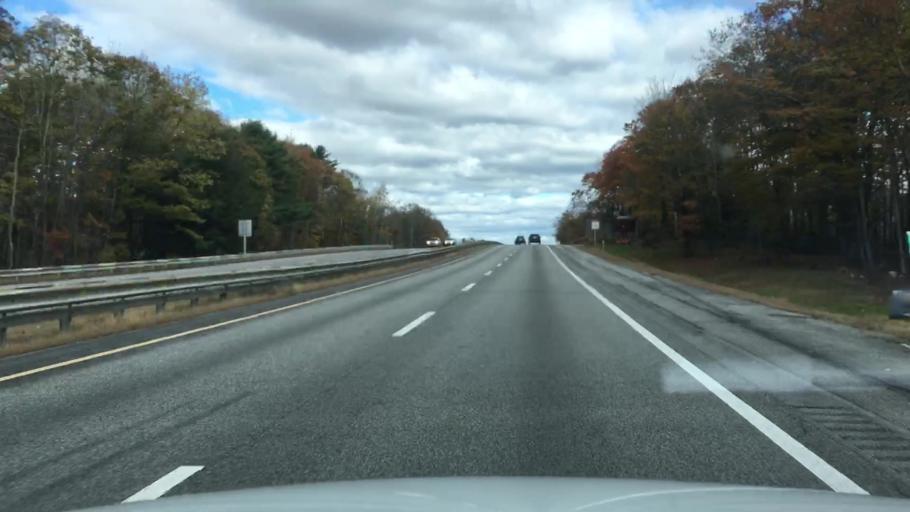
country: US
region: Maine
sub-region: Cumberland County
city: Freeport
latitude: 43.8531
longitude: -70.1140
